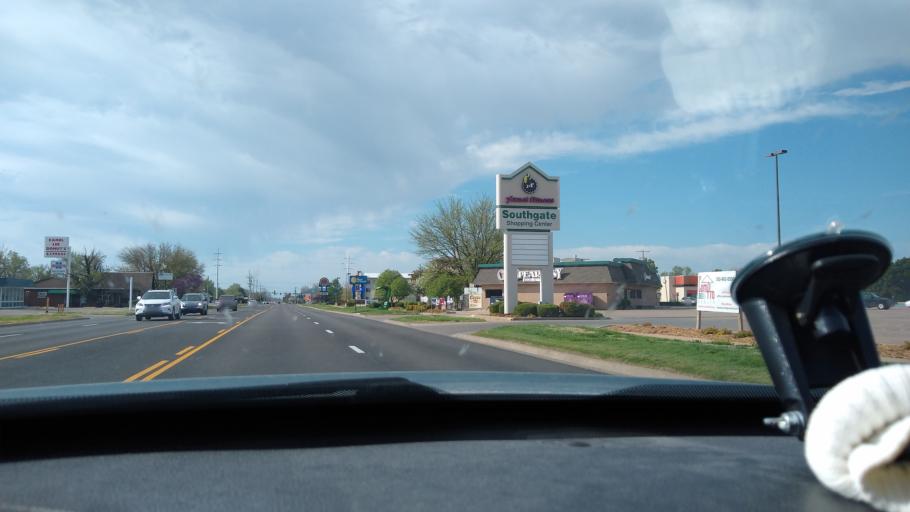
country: US
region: Kansas
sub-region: Saline County
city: Salina
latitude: 38.8086
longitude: -97.5943
